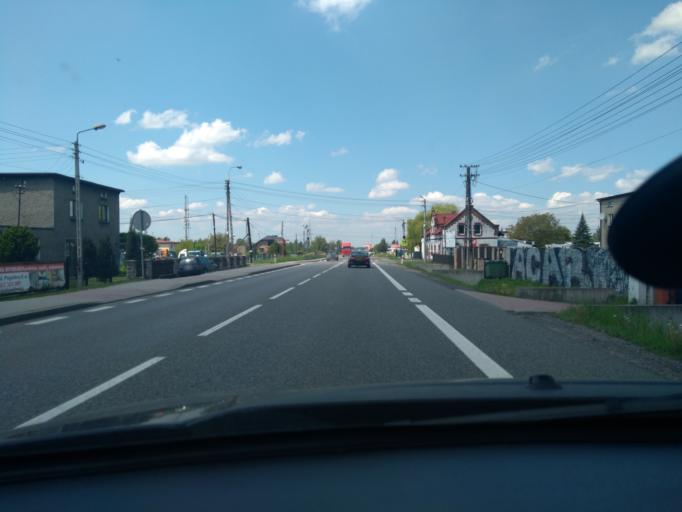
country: PL
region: Silesian Voivodeship
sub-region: Ruda Slaska
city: Ruda Slaska
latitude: 50.2165
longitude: 18.8364
